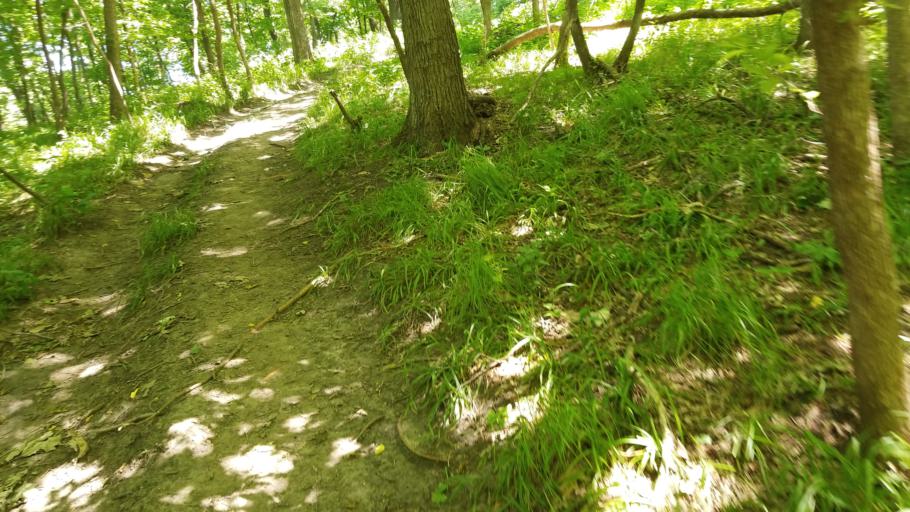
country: US
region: Iowa
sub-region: Pottawattamie County
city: Carter Lake
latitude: 41.3982
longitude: -95.9557
